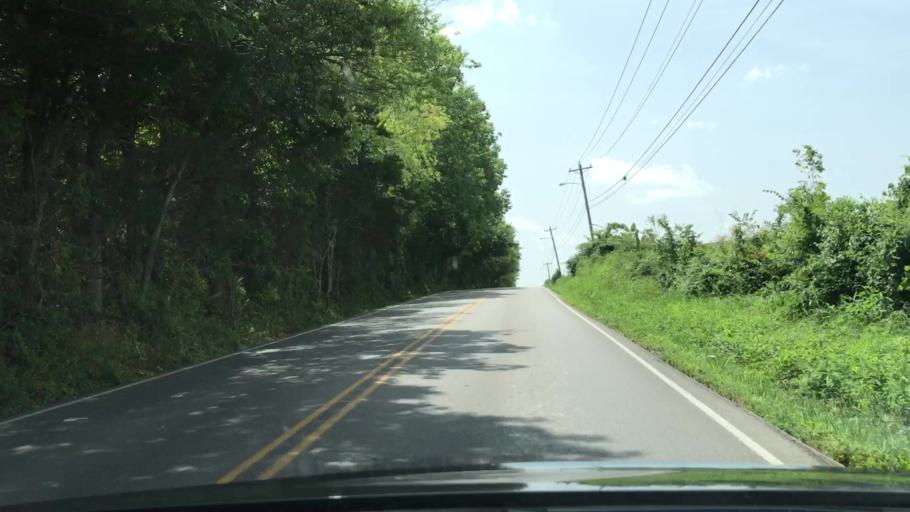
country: US
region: Tennessee
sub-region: Rutherford County
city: La Vergne
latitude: 35.9704
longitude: -86.6002
